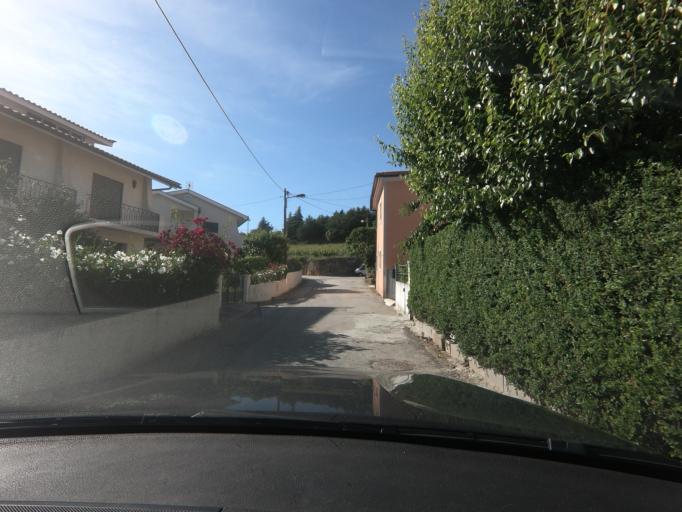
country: PT
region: Vila Real
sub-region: Vila Real
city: Vila Real
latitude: 41.2974
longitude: -7.7100
